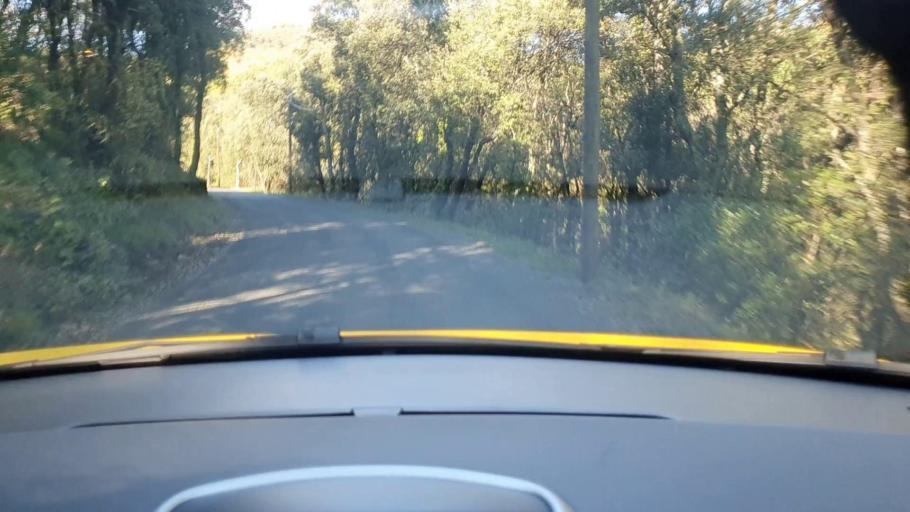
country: FR
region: Languedoc-Roussillon
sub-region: Departement du Gard
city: Le Vigan
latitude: 43.9961
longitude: 3.6280
